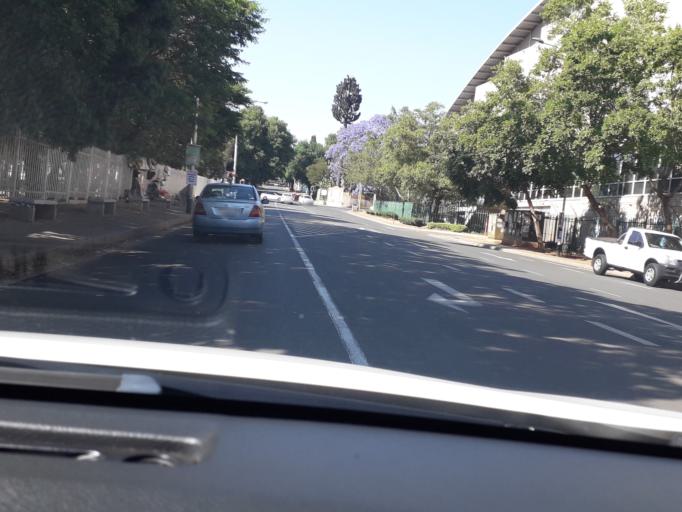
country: ZA
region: Gauteng
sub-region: City of Johannesburg Metropolitan Municipality
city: Johannesburg
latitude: -26.1824
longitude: 28.0066
